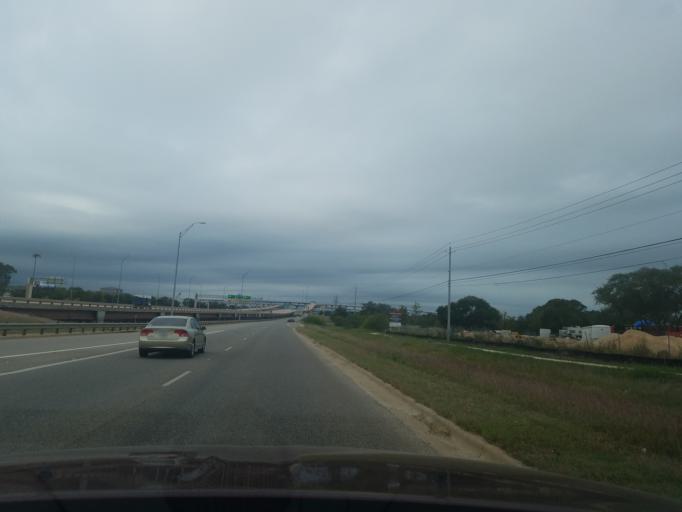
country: US
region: Texas
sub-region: Williamson County
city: Anderson Mill
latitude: 30.4740
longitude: -97.7816
